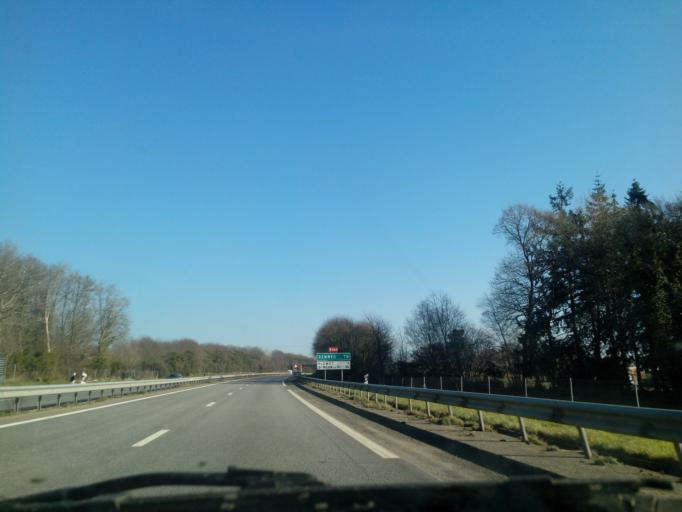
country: FR
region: Brittany
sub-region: Departement des Cotes-d'Armor
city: Saint-Barnabe
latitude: 48.1813
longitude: -2.6733
